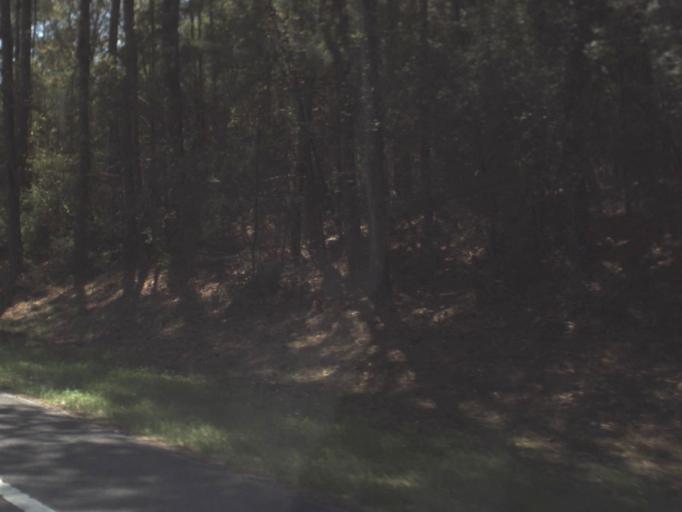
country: US
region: Florida
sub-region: Walton County
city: DeFuniak Springs
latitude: 30.7907
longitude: -85.9586
